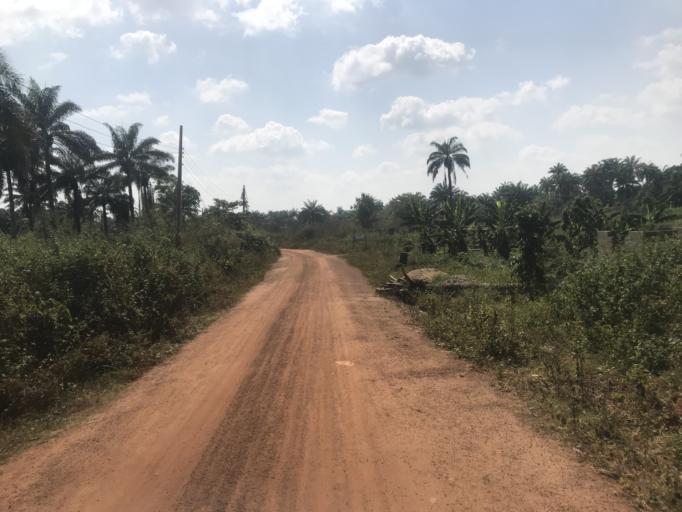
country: NG
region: Osun
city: Iragbiji
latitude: 7.8819
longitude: 4.7005
